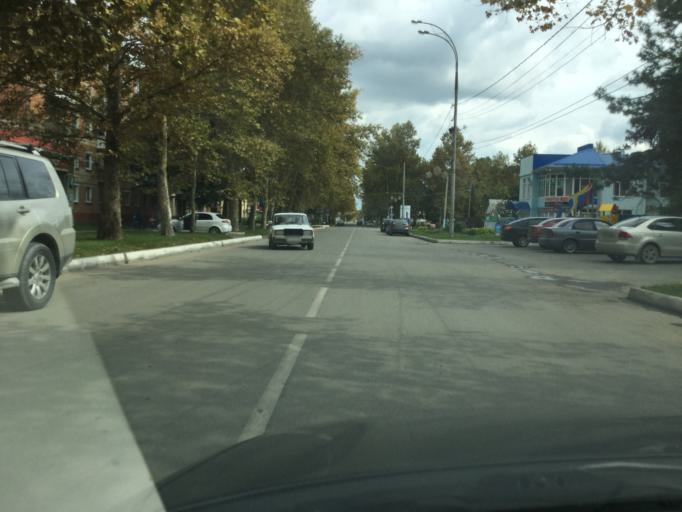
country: RU
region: Krasnodarskiy
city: Slavyansk-na-Kubani
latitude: 45.2570
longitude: 38.1201
